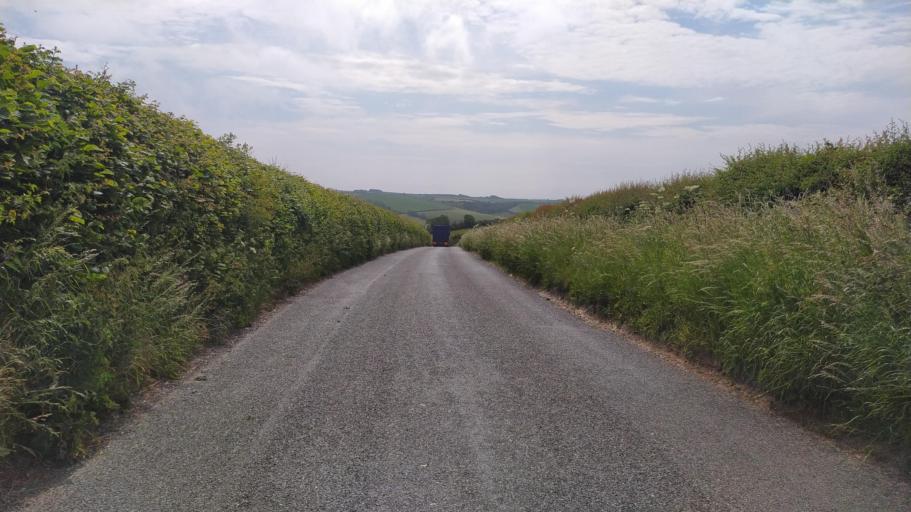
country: GB
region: England
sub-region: Dorset
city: Dorchester
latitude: 50.7999
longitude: -2.5399
